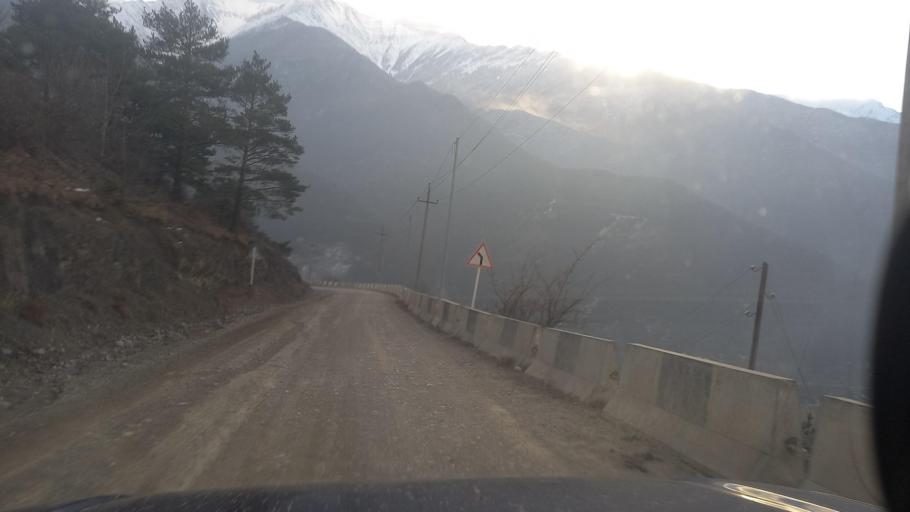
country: RU
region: Ingushetiya
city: Dzhayrakh
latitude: 42.8236
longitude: 44.7051
